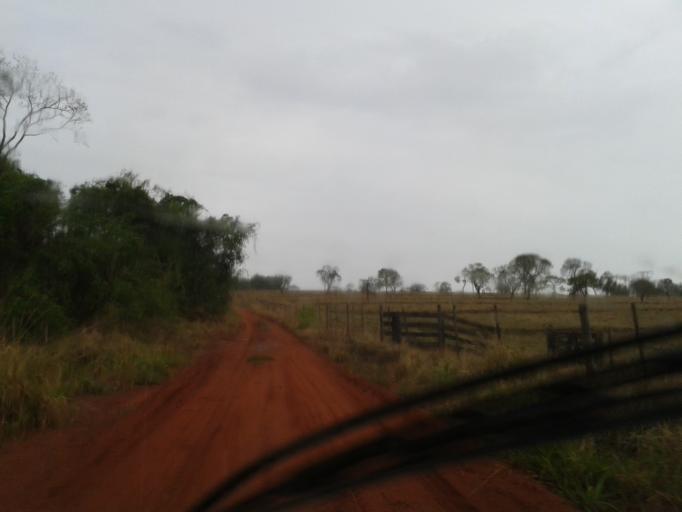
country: BR
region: Minas Gerais
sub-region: Campina Verde
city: Campina Verde
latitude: -19.3544
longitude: -49.5368
